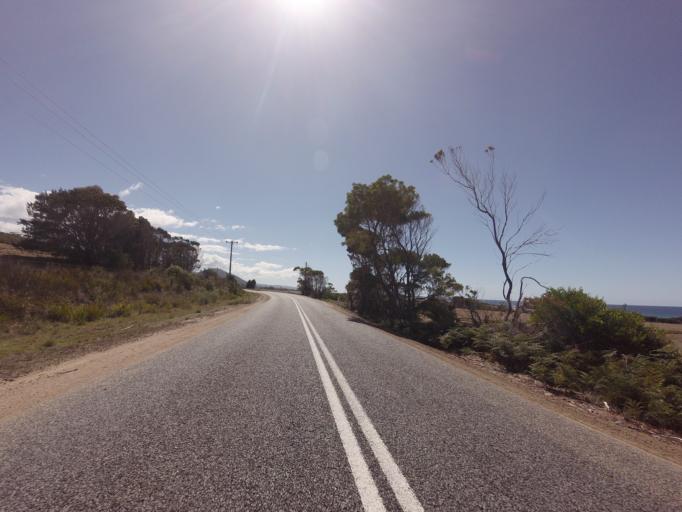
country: AU
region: Tasmania
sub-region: Break O'Day
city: St Helens
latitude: -41.7935
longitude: 148.2626
